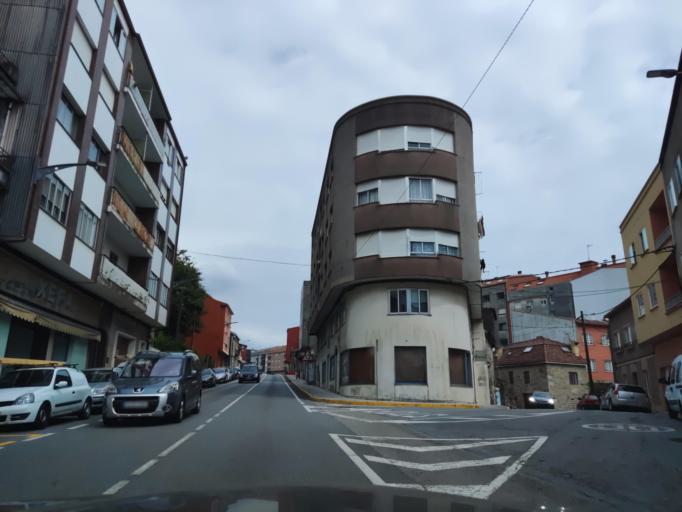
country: ES
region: Galicia
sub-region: Provincia da Coruna
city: Boiro
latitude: 42.6497
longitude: -8.8801
